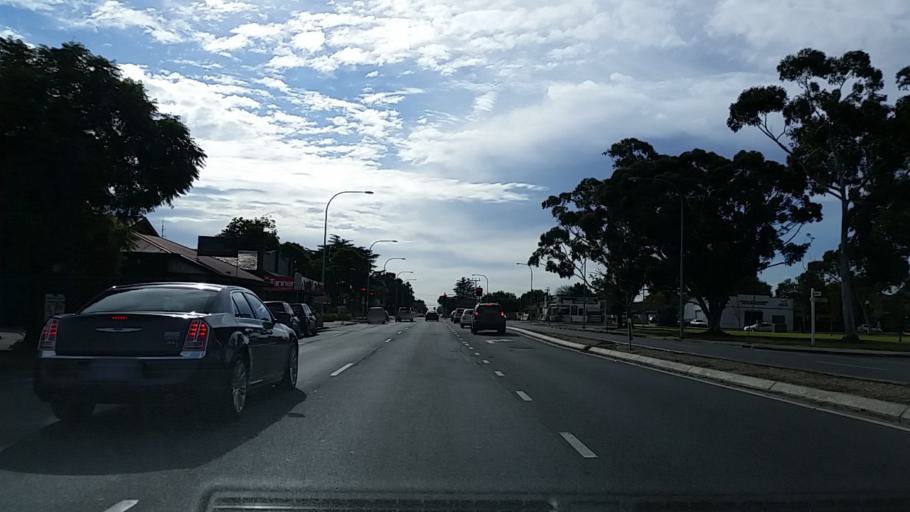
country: AU
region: South Australia
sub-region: Mitcham
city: Clarence Gardens
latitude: -34.9783
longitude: 138.5917
